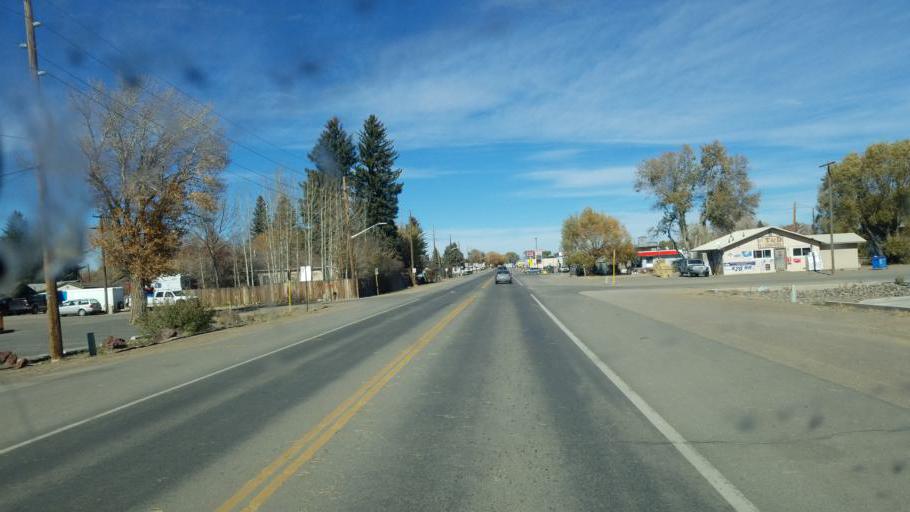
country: US
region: Colorado
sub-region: Conejos County
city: Conejos
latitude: 37.2726
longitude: -105.9626
